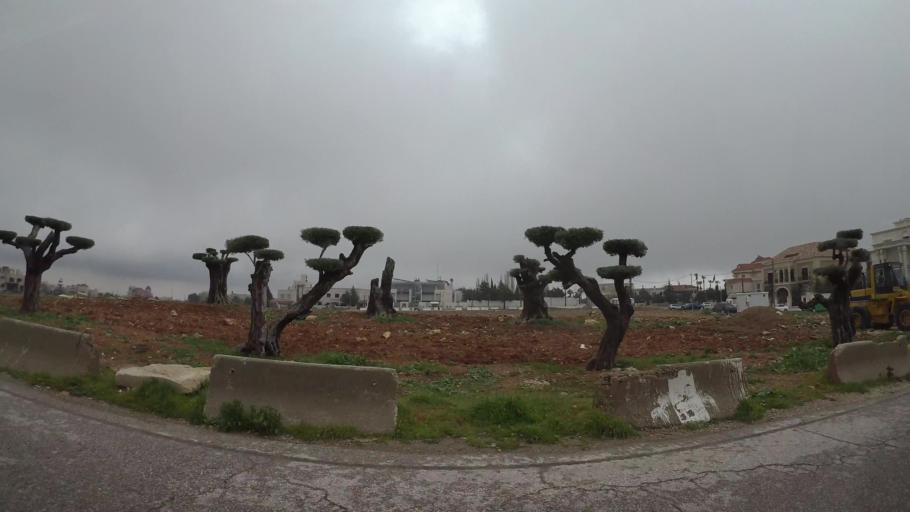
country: JO
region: Amman
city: Al Bunayyat ash Shamaliyah
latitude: 31.9387
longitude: 35.8763
